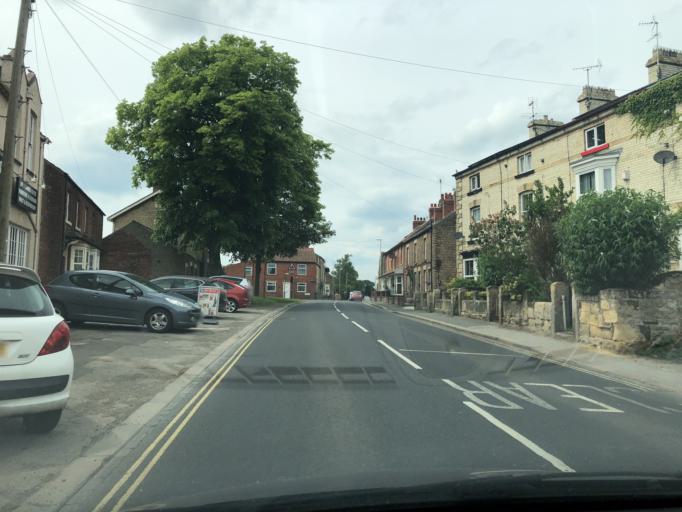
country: GB
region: England
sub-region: North Yorkshire
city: Pickering
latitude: 54.2450
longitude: -0.7811
